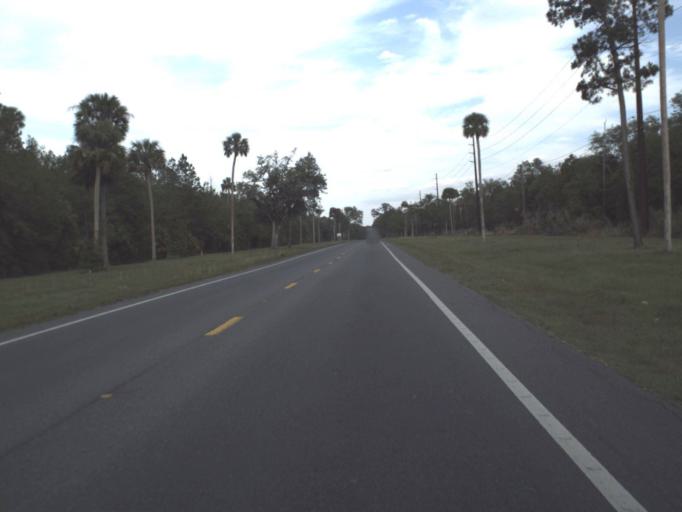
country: US
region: Florida
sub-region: Marion County
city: Silver Springs Shores
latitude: 29.2172
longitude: -82.0077
